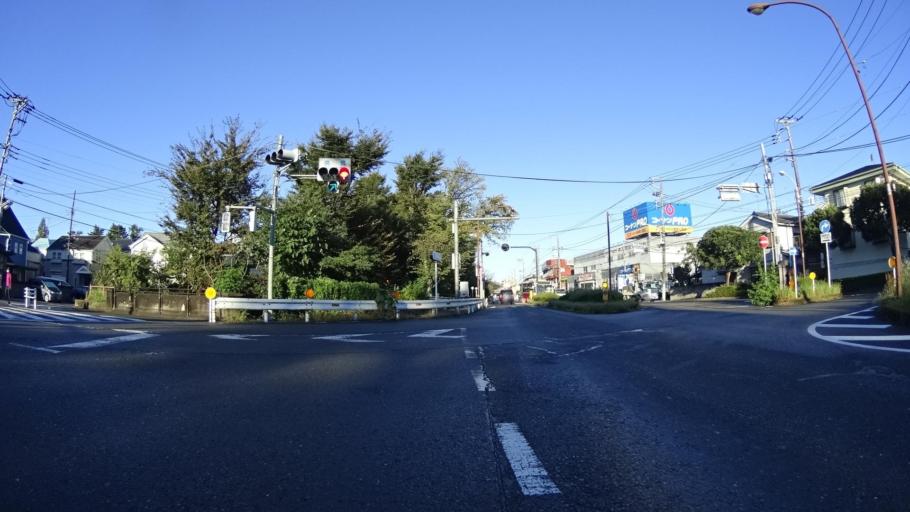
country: JP
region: Tokyo
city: Nishi-Tokyo-shi
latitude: 35.7109
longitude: 139.5372
